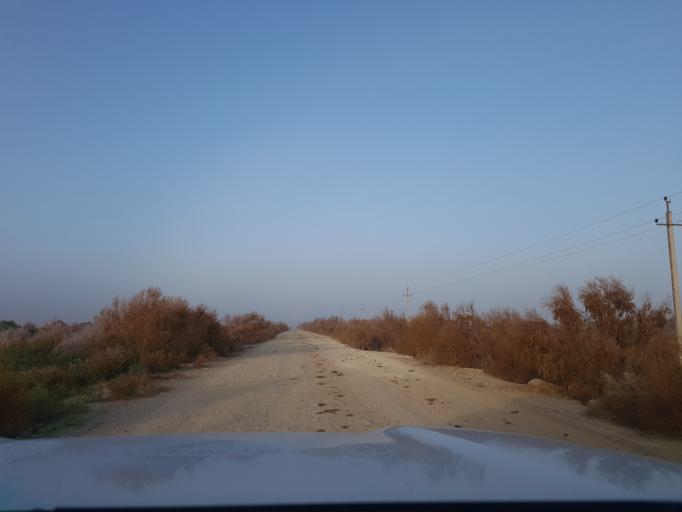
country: TM
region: Dasoguz
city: Koeneuergench
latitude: 41.8463
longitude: 58.3822
